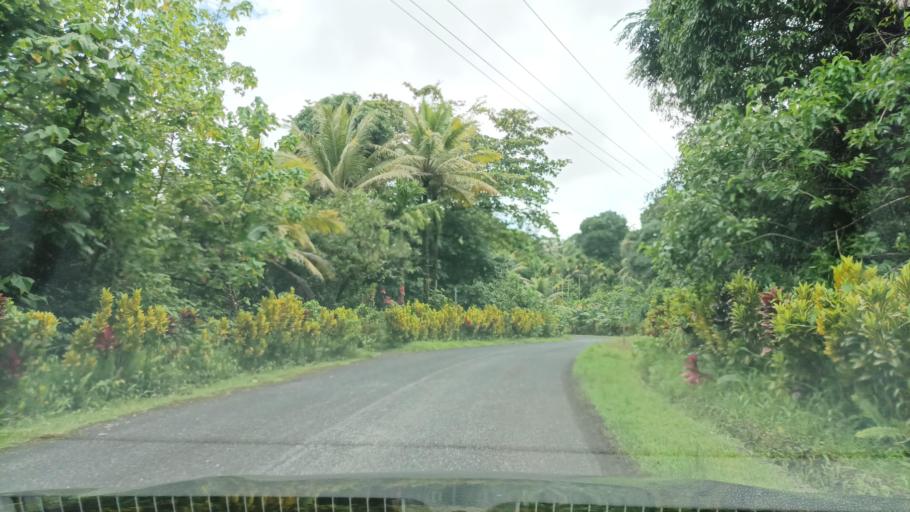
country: FM
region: Pohnpei
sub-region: Madolenihm Municipality
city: Madolenihm Municipality Government
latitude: 6.8243
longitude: 158.2985
